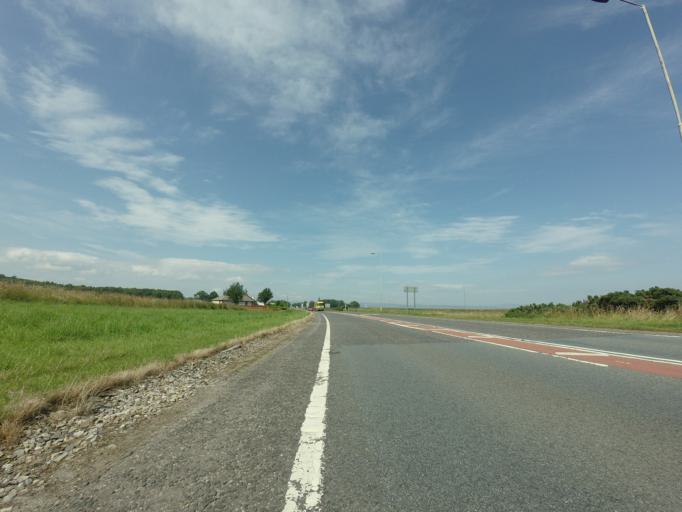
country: GB
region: Scotland
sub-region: Highland
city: Tain
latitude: 57.8185
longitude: -4.0716
